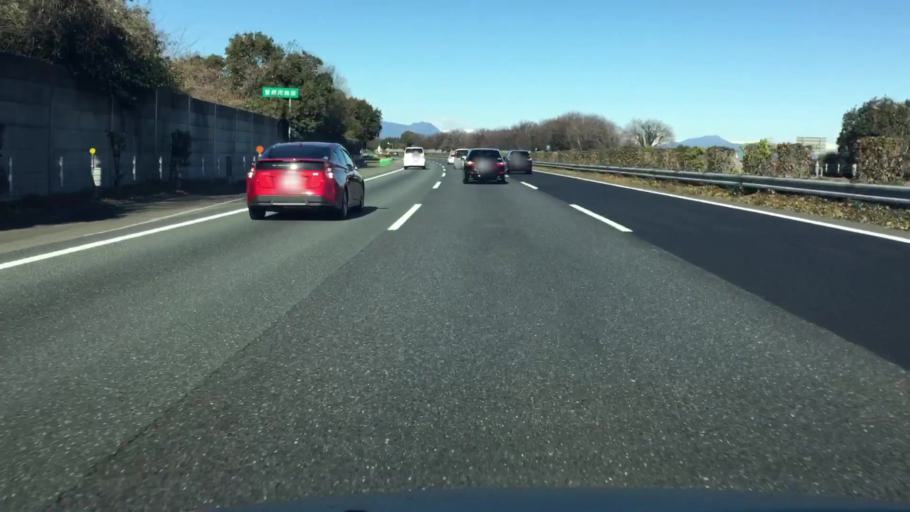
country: JP
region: Saitama
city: Honjo
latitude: 36.2438
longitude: 139.1432
